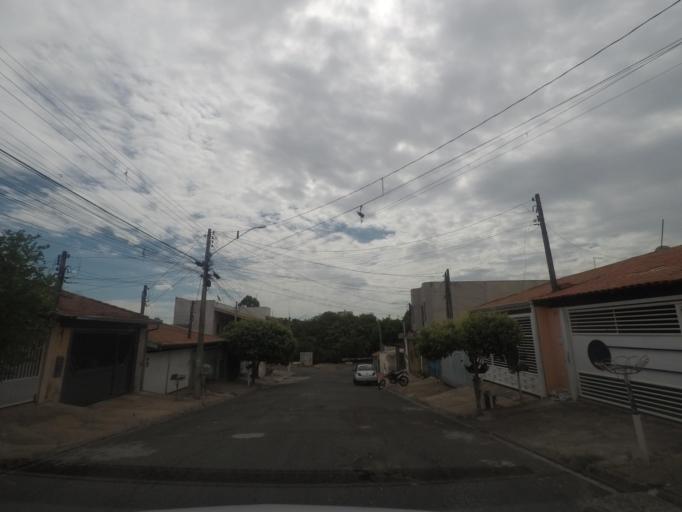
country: BR
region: Sao Paulo
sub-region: Nova Odessa
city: Nova Odessa
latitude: -22.7981
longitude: -47.2831
